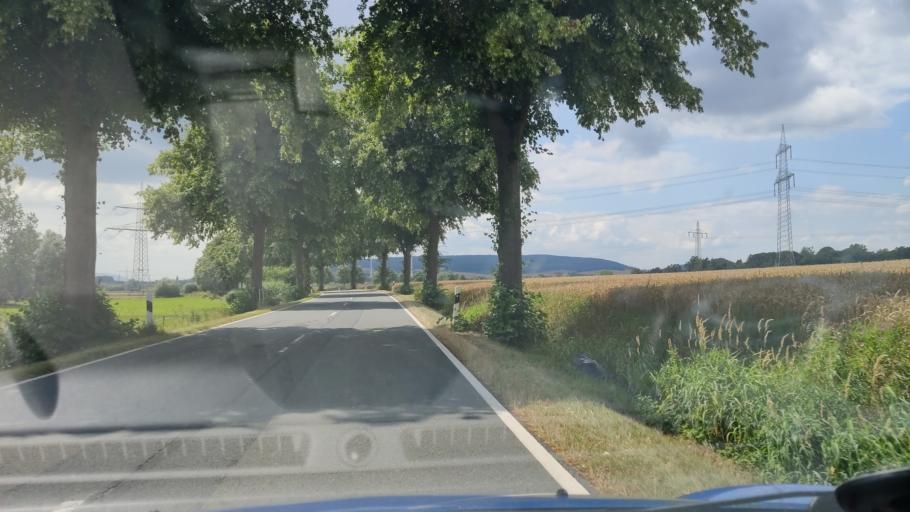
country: DE
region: Lower Saxony
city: Bad Munder am Deister
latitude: 52.1414
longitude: 9.4704
